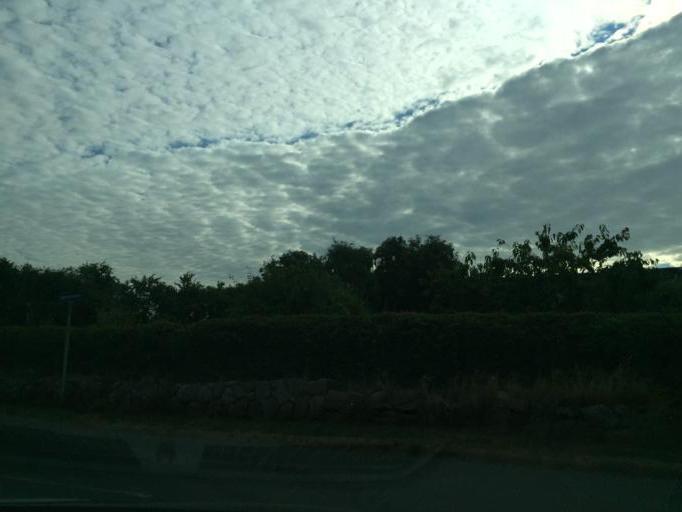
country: DK
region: South Denmark
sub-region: Assens Kommune
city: Assens
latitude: 55.2734
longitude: 9.9769
